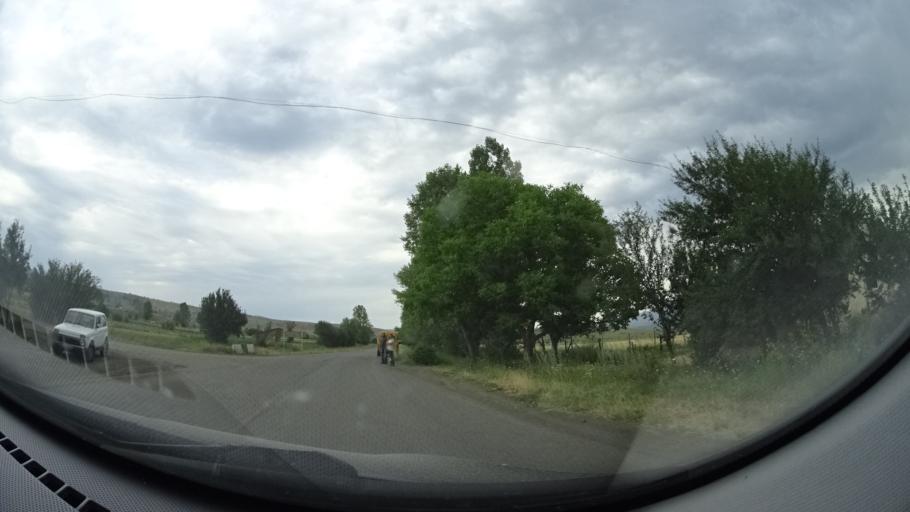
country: GE
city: Abastumani
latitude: 41.6642
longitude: 42.7783
